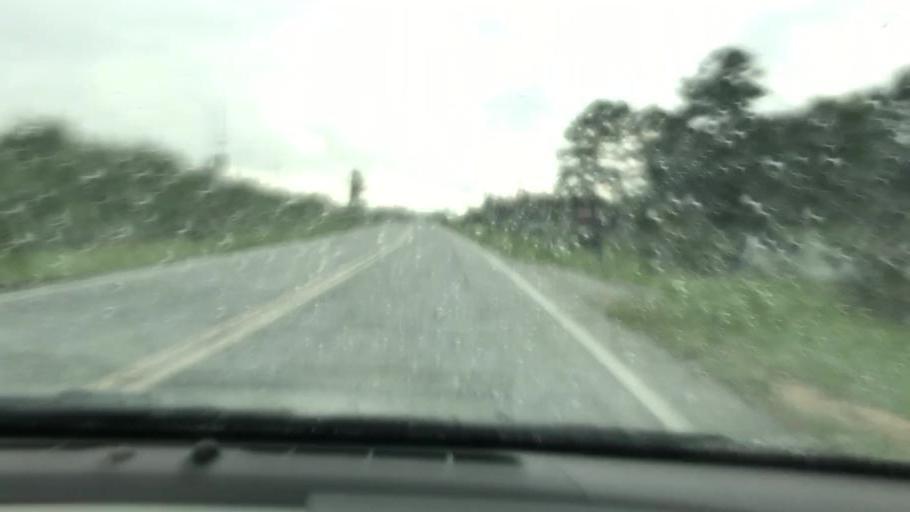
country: US
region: Georgia
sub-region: Clay County
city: Fort Gaines
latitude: 31.6678
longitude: -85.0469
